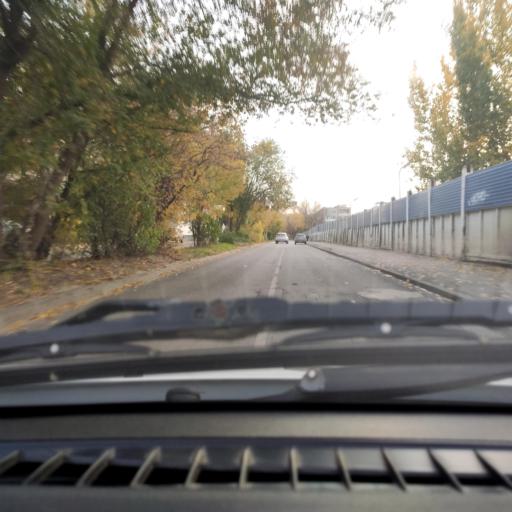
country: RU
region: Samara
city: Zhigulevsk
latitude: 53.4687
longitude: 49.5302
